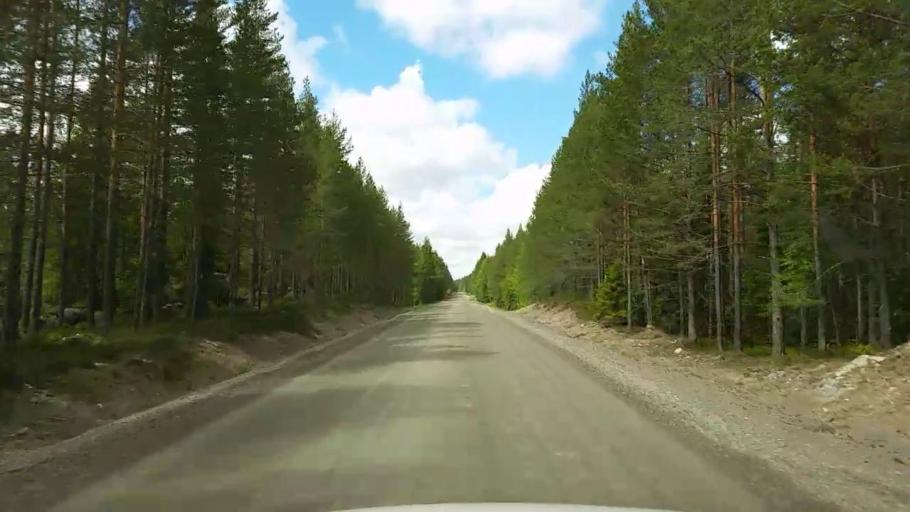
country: SE
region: Gaevleborg
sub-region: Bollnas Kommun
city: Vittsjo
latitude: 61.0346
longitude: 16.3653
